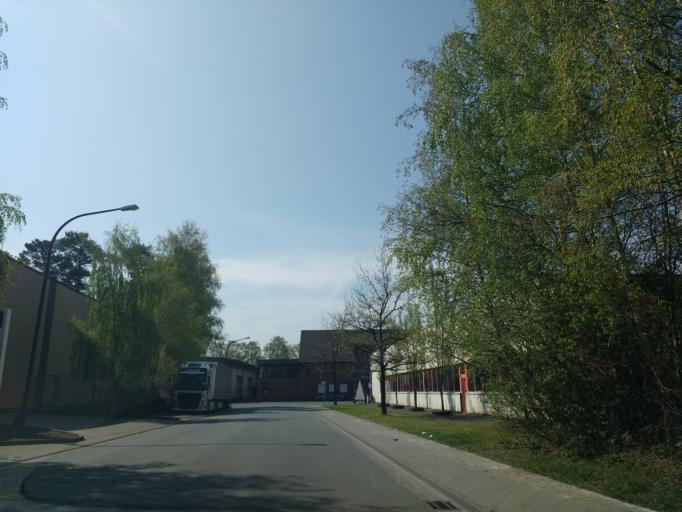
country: DE
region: North Rhine-Westphalia
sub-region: Regierungsbezirk Detmold
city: Hovelhof
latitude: 51.8326
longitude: 8.6487
